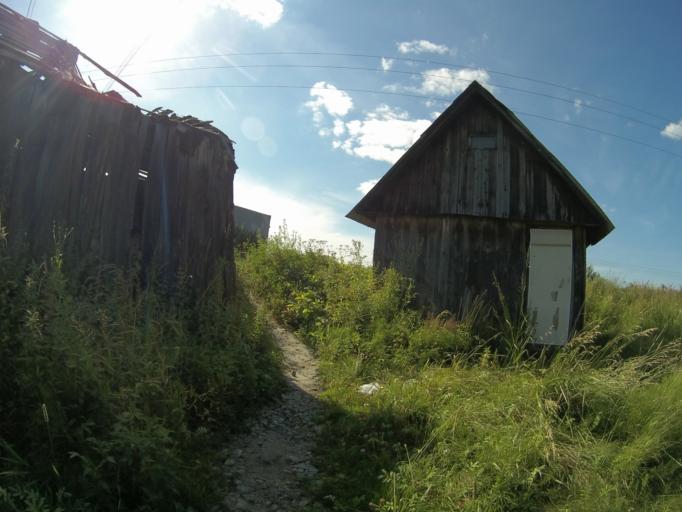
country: RU
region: Vladimir
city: Vorsha
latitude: 56.0982
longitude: 40.1914
